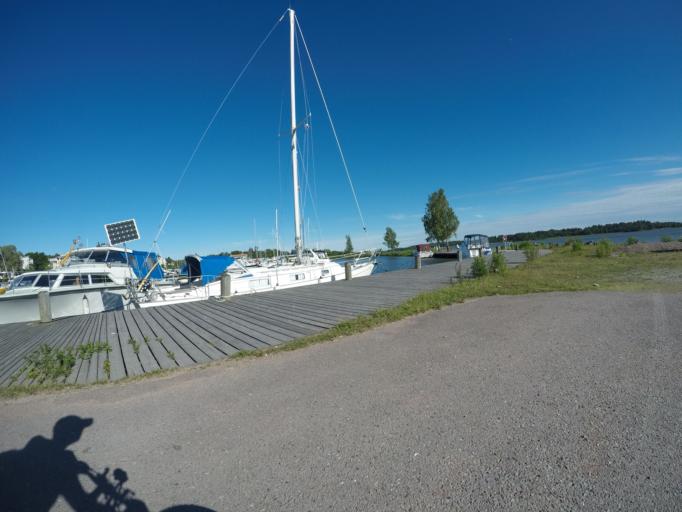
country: SE
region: Vaestmanland
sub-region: Vasteras
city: Vasteras
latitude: 59.5970
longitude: 16.5824
